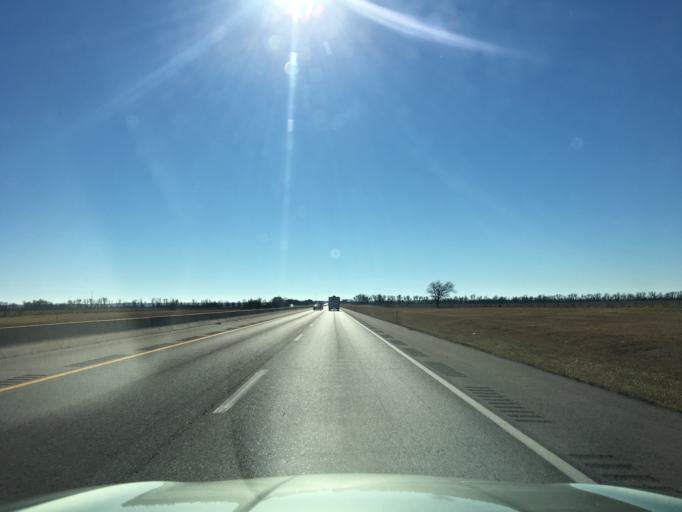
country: US
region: Kansas
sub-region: Sumner County
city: Wellington
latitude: 37.0419
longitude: -97.3384
